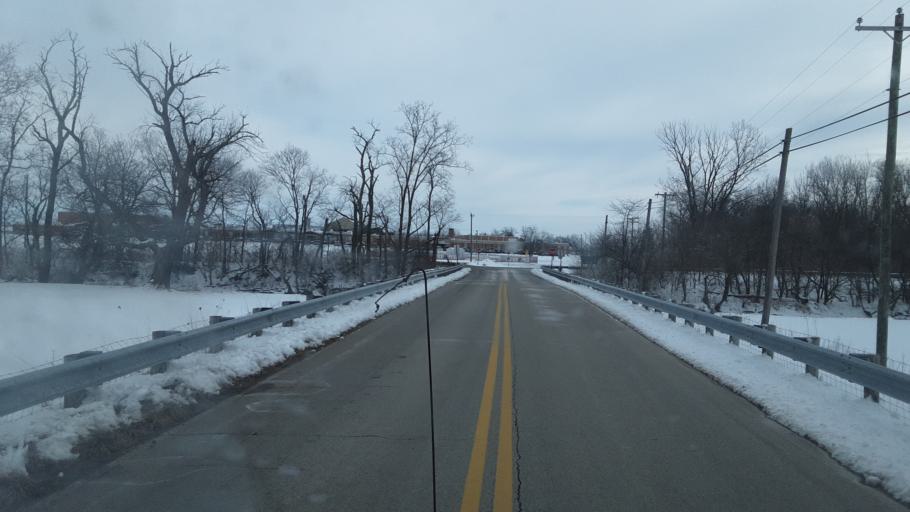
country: US
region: Ohio
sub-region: Union County
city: Marysville
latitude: 40.1607
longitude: -83.3959
